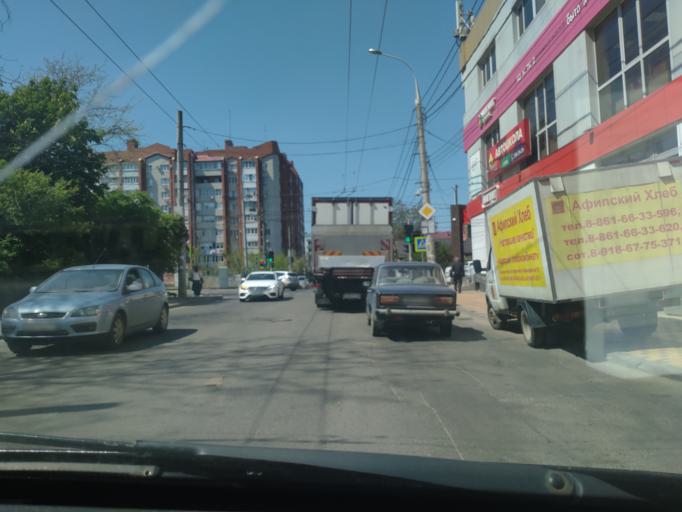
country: RU
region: Krasnodarskiy
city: Krasnodar
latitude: 45.0656
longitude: 39.0224
